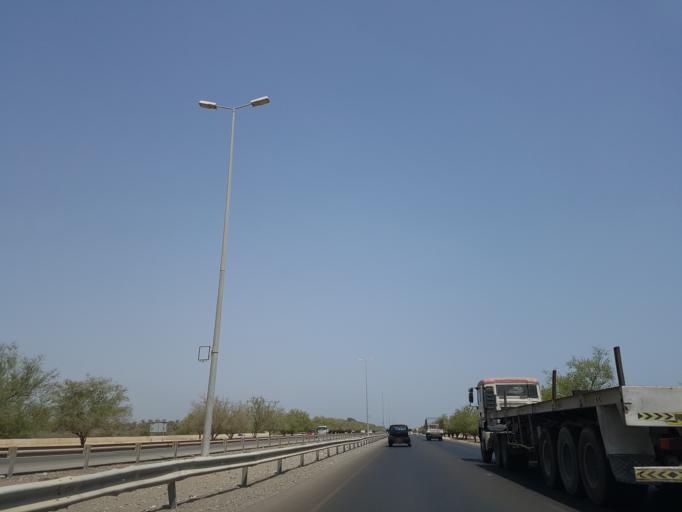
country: OM
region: Al Batinah
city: Saham
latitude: 24.1595
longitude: 56.8649
